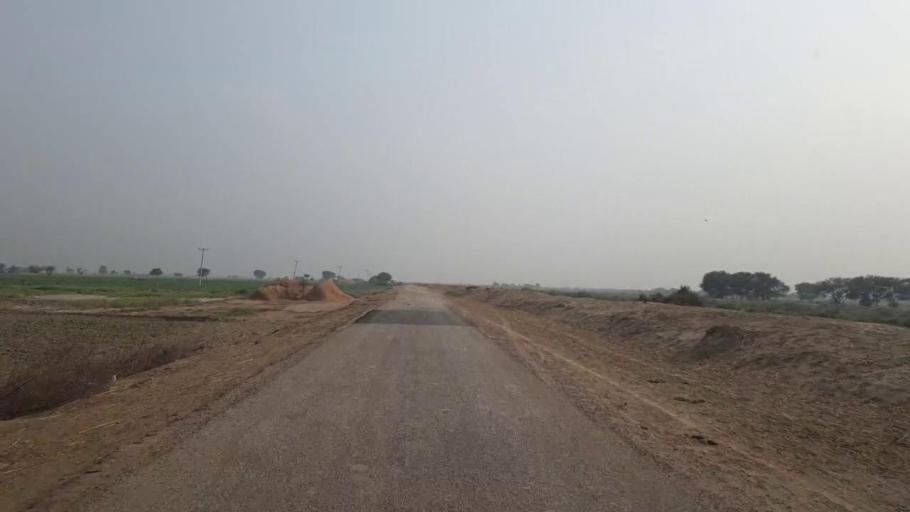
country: PK
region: Sindh
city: Mirpur Batoro
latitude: 24.5741
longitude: 68.3975
